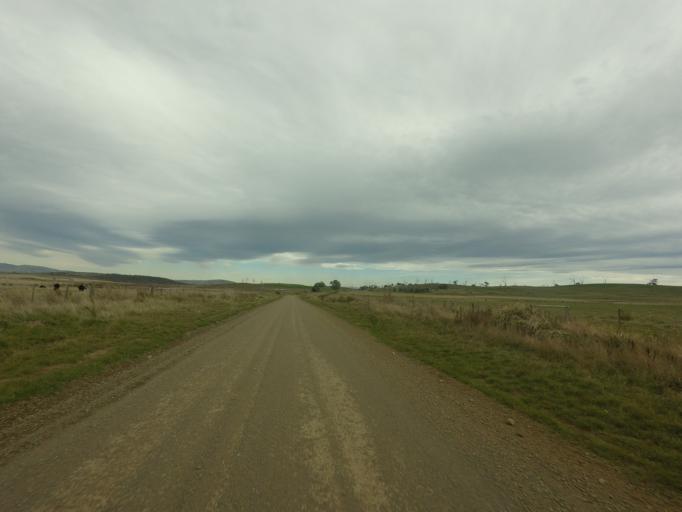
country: AU
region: Tasmania
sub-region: Derwent Valley
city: New Norfolk
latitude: -42.3934
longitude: 146.9743
